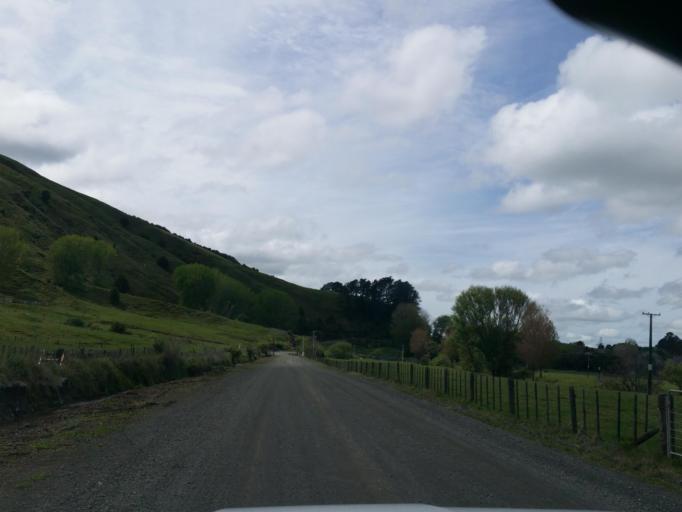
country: NZ
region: Northland
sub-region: Whangarei
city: Maungatapere
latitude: -35.8976
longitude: 174.0884
